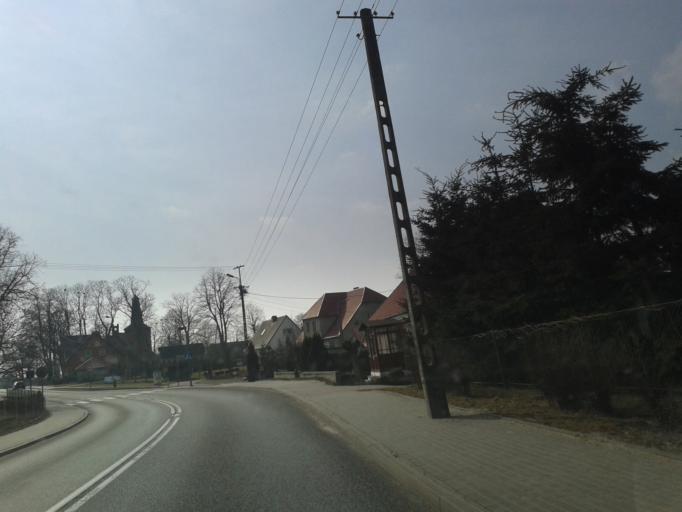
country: PL
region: Pomeranian Voivodeship
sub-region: Powiat czluchowski
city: Debrzno
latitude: 53.5992
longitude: 17.1345
